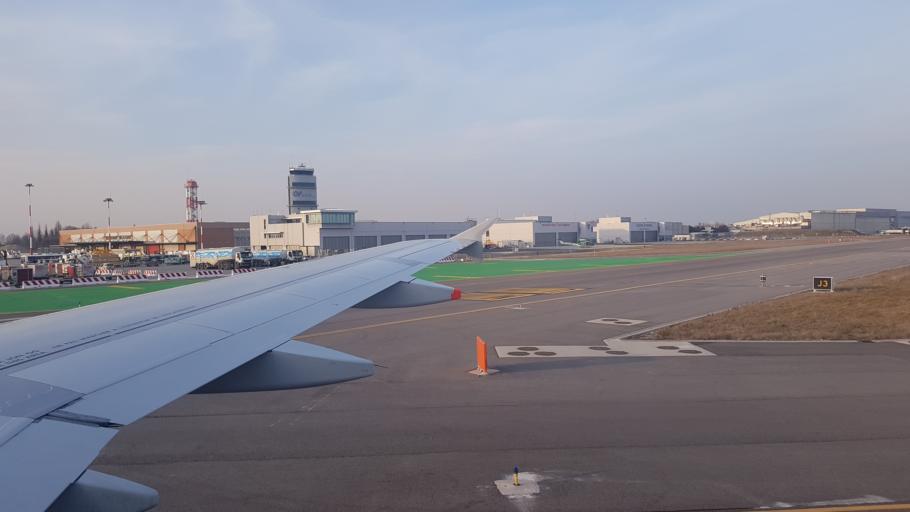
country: IT
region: Veneto
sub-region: Provincia di Venezia
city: Tessera
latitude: 45.5062
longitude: 12.3484
